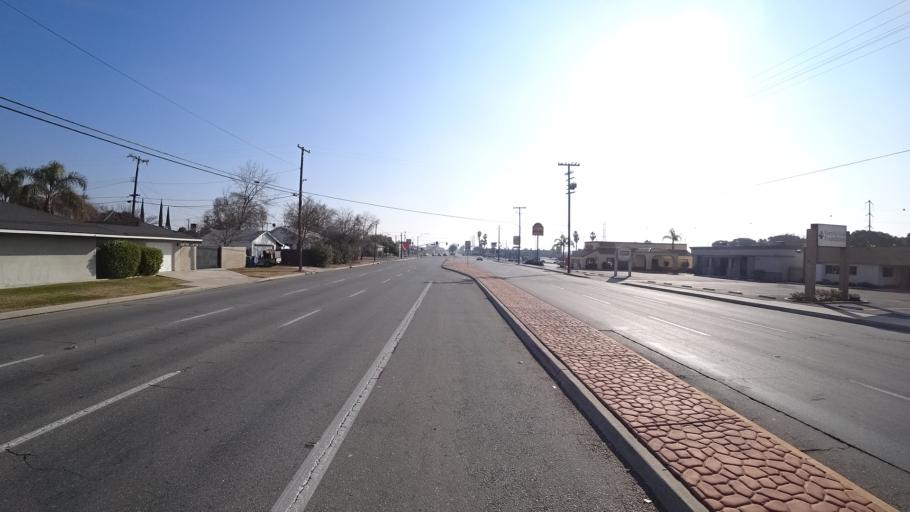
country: US
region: California
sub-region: Kern County
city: Bakersfield
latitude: 35.3919
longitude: -119.0029
